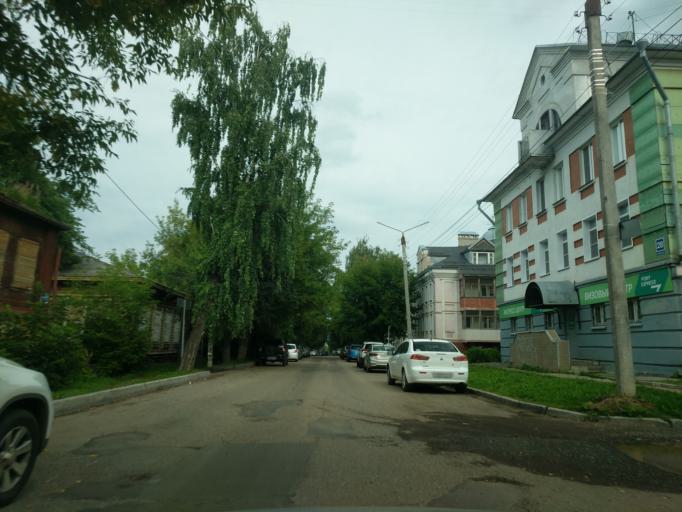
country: RU
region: Kirov
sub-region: Kirovo-Chepetskiy Rayon
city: Kirov
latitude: 58.5963
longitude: 49.6756
